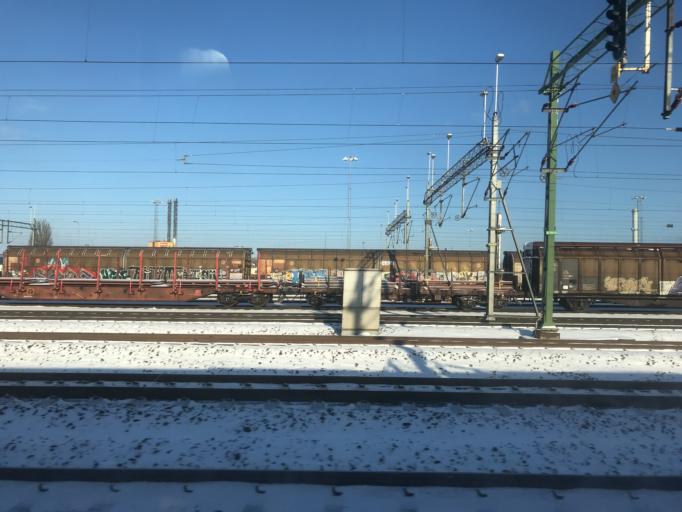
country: SE
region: Skane
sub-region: Burlovs Kommun
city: Arloev
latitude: 55.6185
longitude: 13.0472
